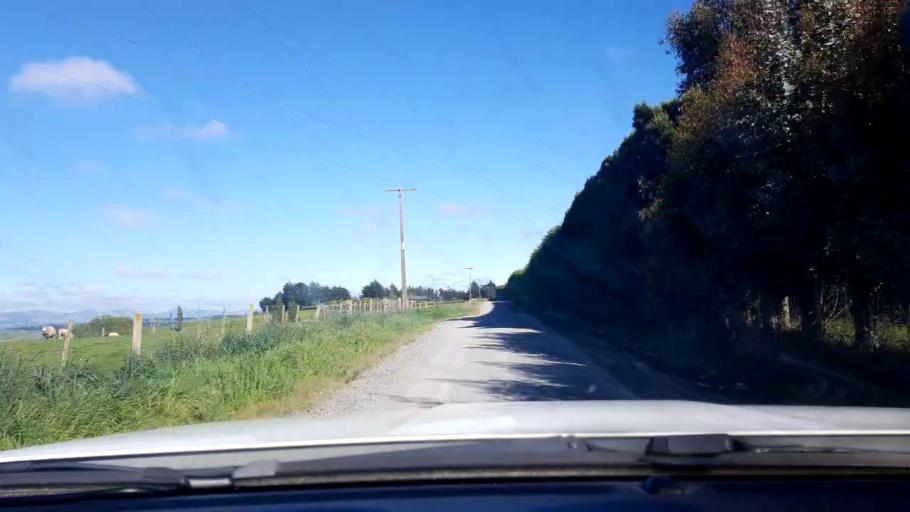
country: NZ
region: Otago
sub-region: Clutha District
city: Balclutha
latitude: -46.2242
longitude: 169.7655
